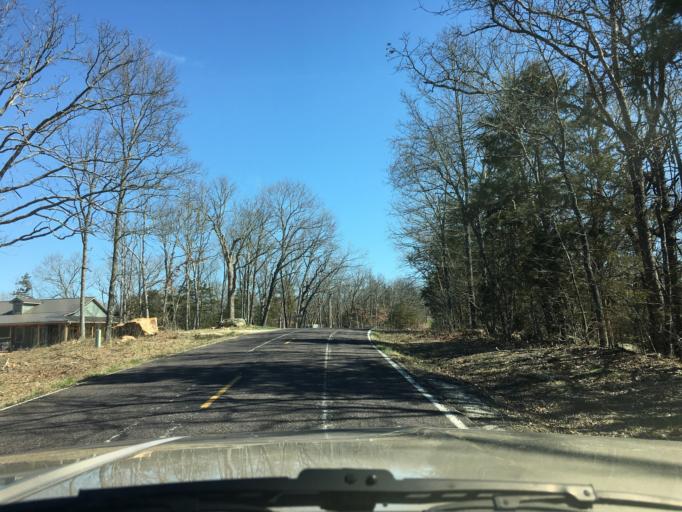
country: US
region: Missouri
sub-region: Franklin County
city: New Haven
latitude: 38.5361
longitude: -91.3309
